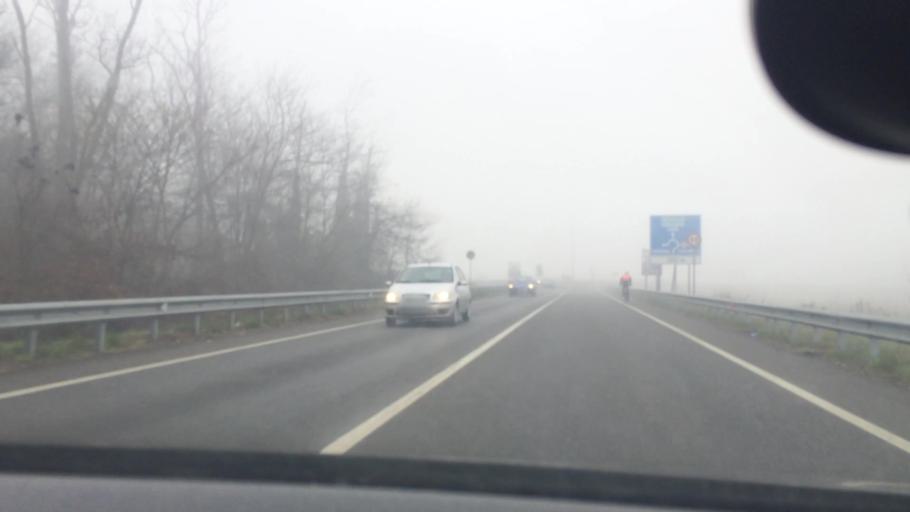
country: IT
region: Lombardy
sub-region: Provincia di Monza e Brianza
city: Ceriano Laghetto
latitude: 45.6276
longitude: 9.0603
